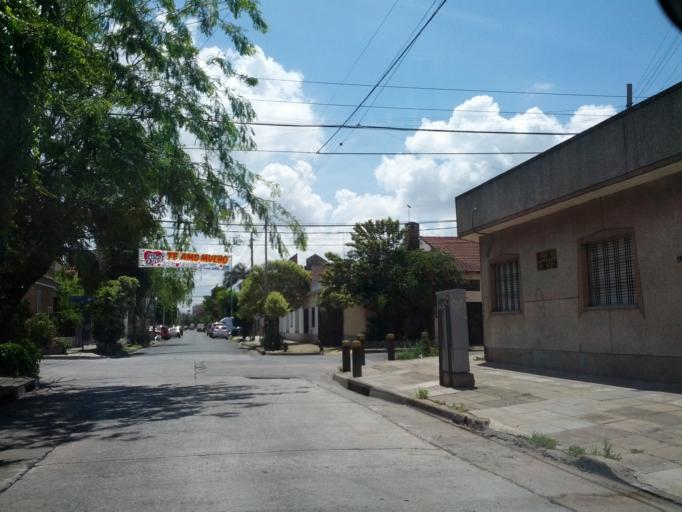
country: AR
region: Buenos Aires
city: San Justo
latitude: -34.6491
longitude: -58.5523
